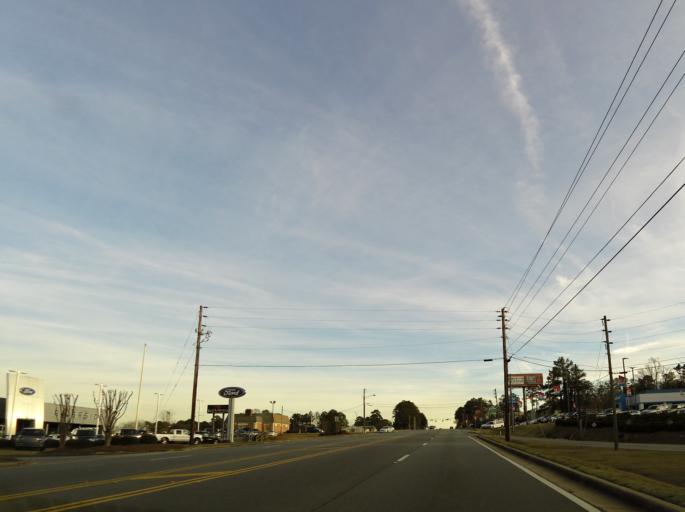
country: US
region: Georgia
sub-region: Bibb County
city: Macon
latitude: 32.8580
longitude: -83.6468
